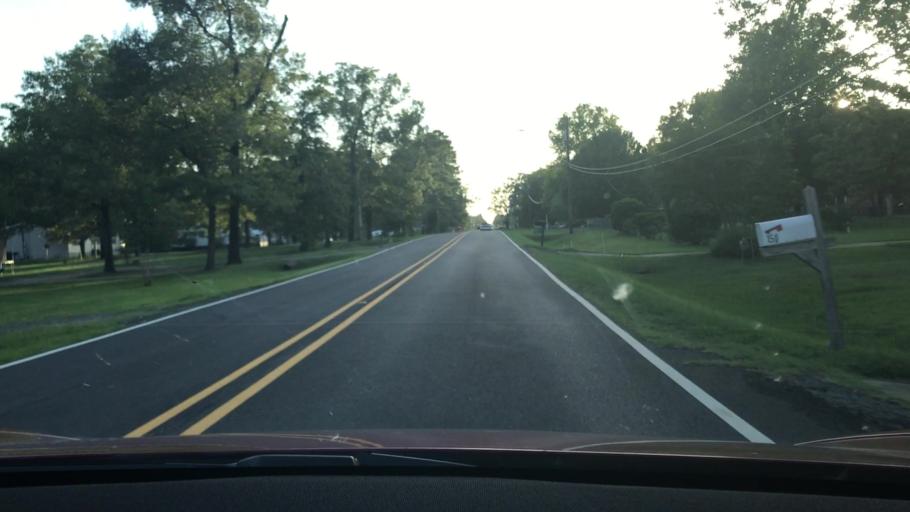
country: US
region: Louisiana
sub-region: Bossier Parish
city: Bossier City
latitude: 32.3909
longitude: -93.7421
